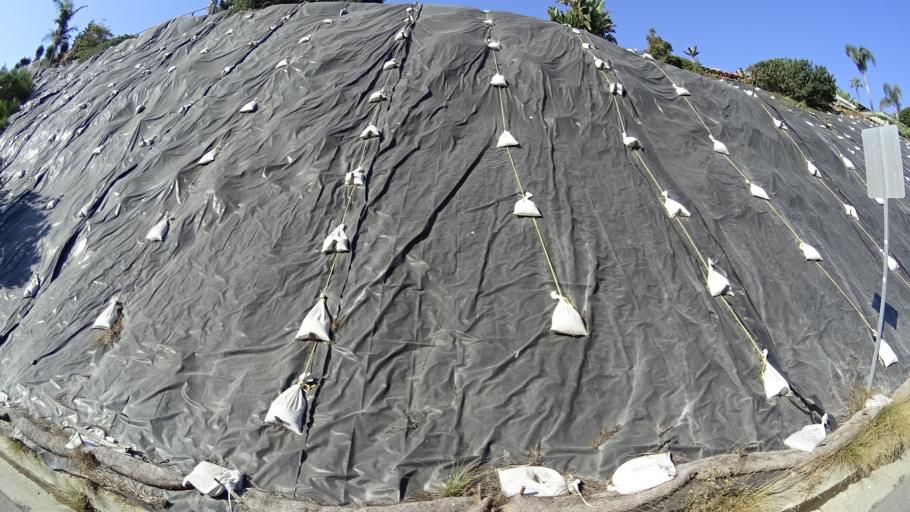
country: US
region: California
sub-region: Orange County
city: San Clemente
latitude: 33.4473
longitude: -117.6467
